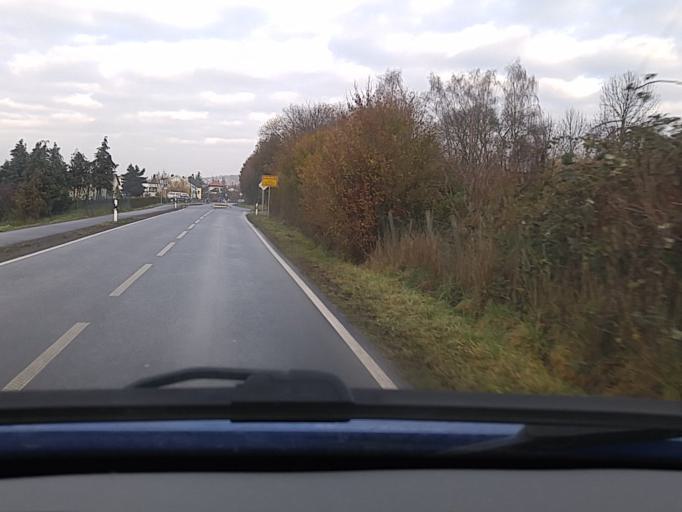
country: DE
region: Hesse
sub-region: Regierungsbezirk Darmstadt
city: Bad Nauheim
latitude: 50.3923
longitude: 8.7528
